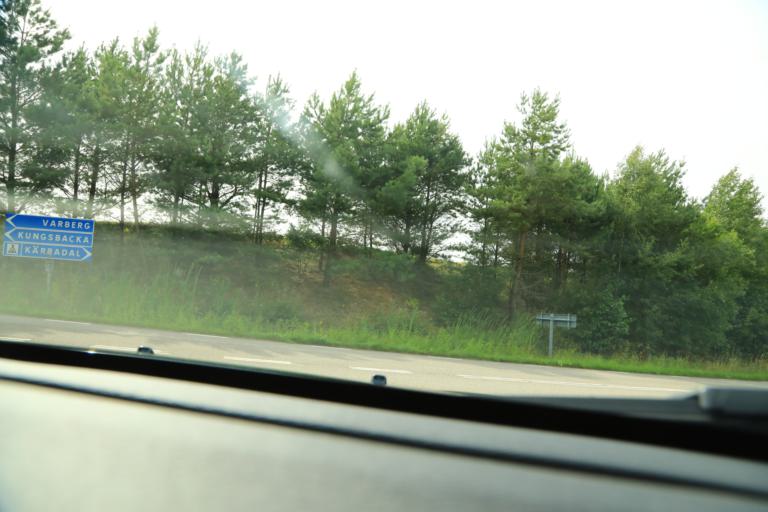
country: SE
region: Halland
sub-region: Varbergs Kommun
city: Varberg
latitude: 57.1824
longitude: 12.2275
